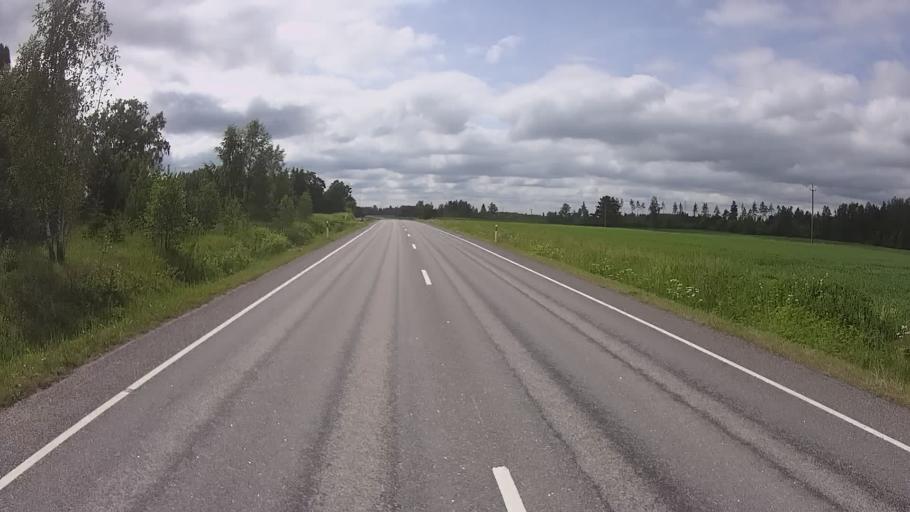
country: EE
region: Polvamaa
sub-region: Polva linn
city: Polva
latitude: 57.9969
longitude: 27.0592
